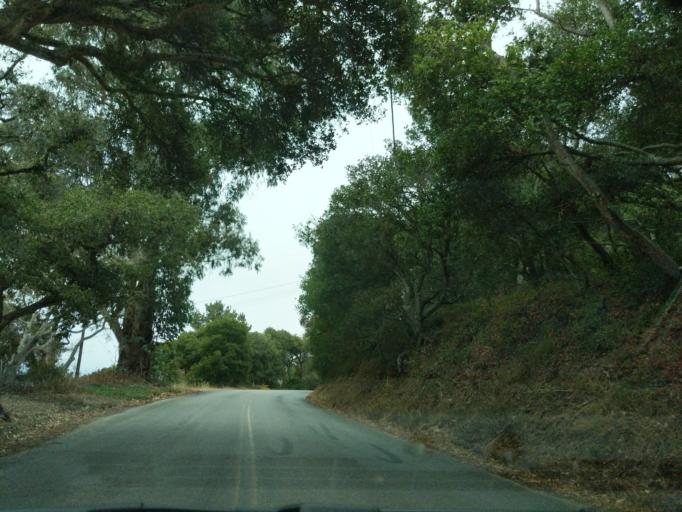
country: US
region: California
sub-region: Monterey County
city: Prunedale
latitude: 36.7890
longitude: -121.6968
